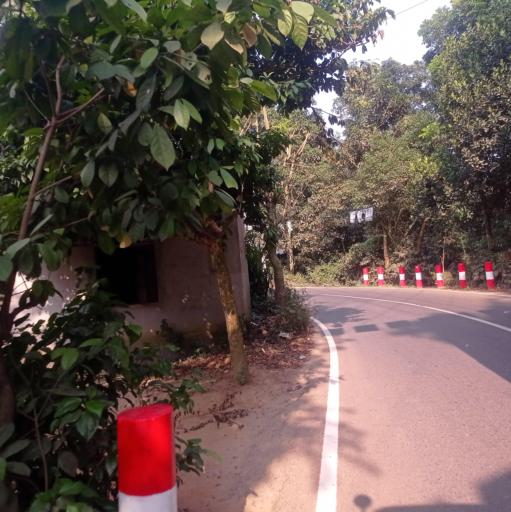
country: BD
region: Dhaka
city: Bhairab Bazar
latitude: 24.0439
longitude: 90.8346
